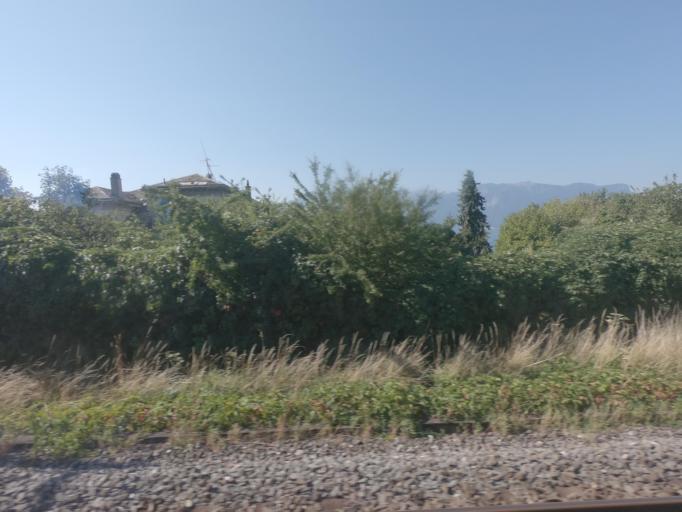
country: CH
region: Vaud
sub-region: Riviera-Pays-d'Enhaut District
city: Chardonne
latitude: 46.4691
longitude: 6.8306
